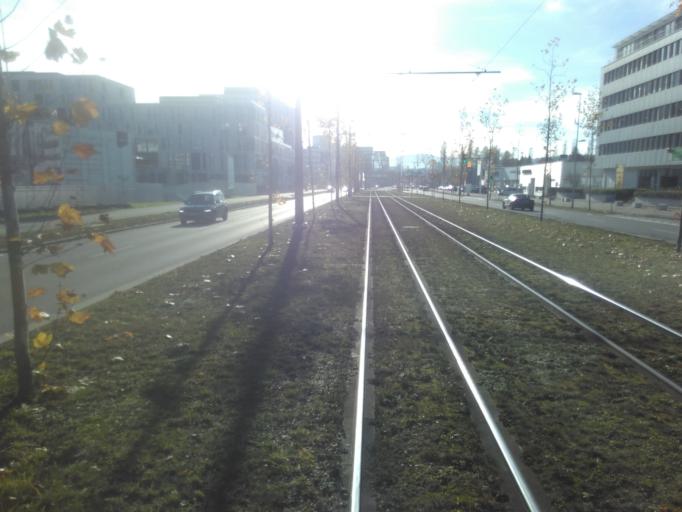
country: CH
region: Zurich
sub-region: Bezirk Buelach
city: Glattbrugg
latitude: 47.4225
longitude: 8.5584
